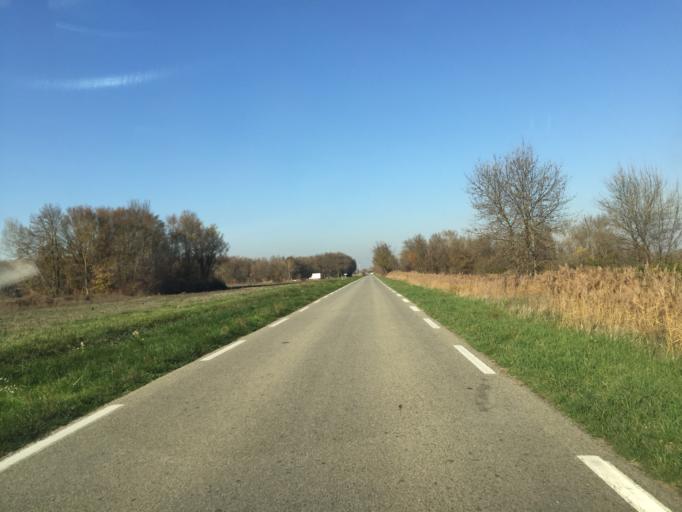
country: FR
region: Provence-Alpes-Cote d'Azur
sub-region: Departement du Vaucluse
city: Entraigues-sur-la-Sorgue
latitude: 44.0235
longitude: 4.9172
